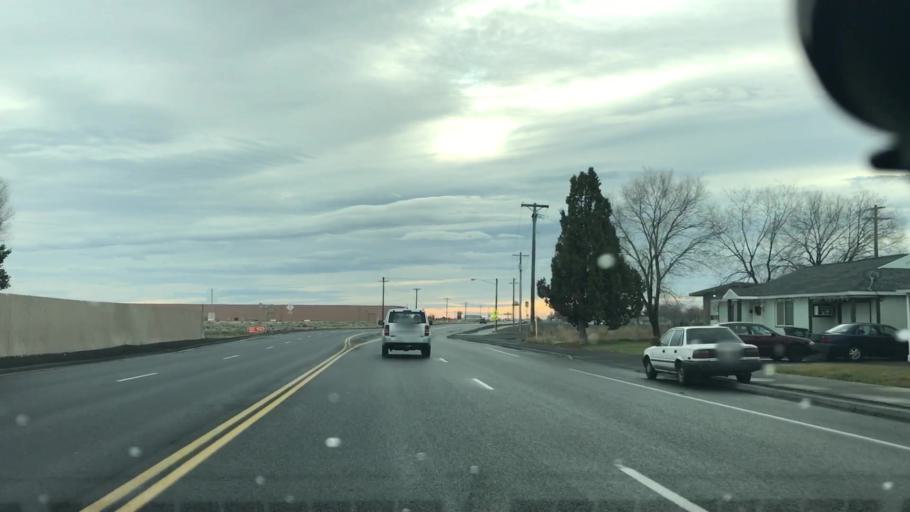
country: US
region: Washington
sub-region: Grant County
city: Moses Lake North
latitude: 47.1752
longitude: -119.3199
